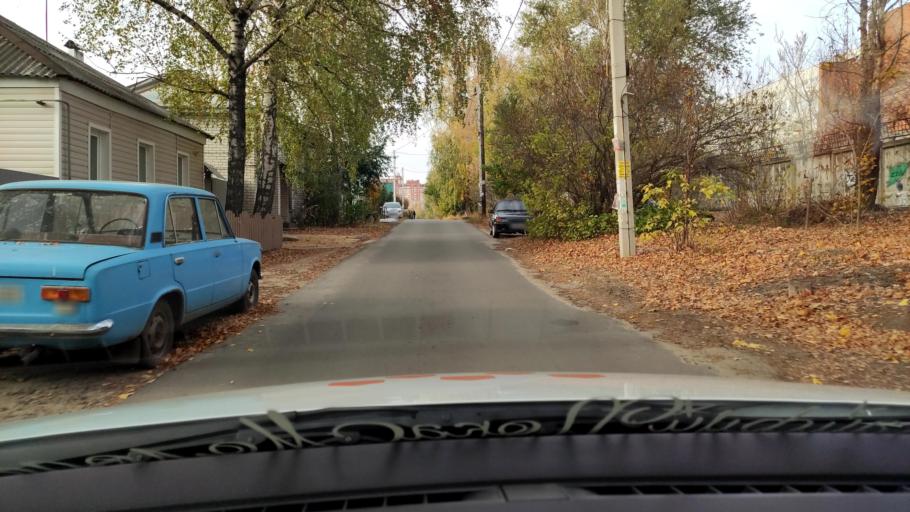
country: RU
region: Voronezj
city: Voronezh
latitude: 51.6421
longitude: 39.1989
